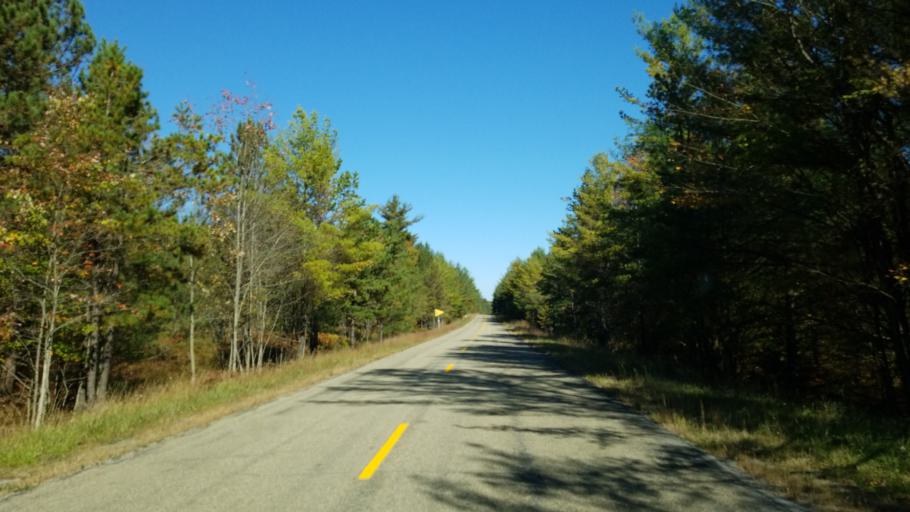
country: US
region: Pennsylvania
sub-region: Clearfield County
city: Shiloh
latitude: 41.2618
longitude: -78.2880
